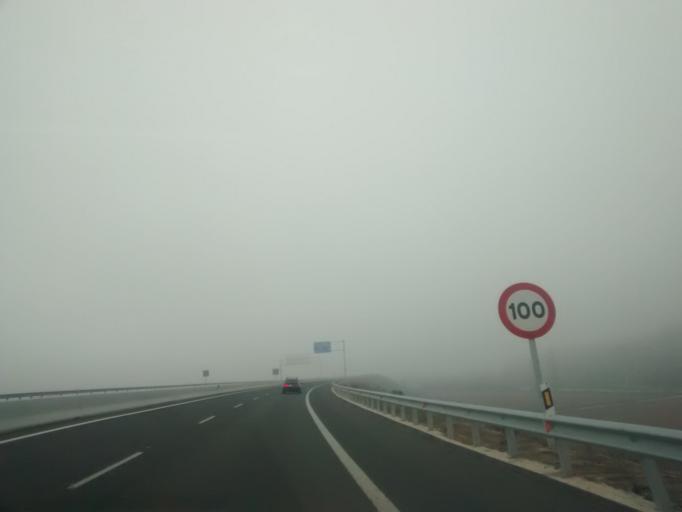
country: ES
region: La Rioja
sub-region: Provincia de La Rioja
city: Murillo de Rio Leza
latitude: 42.4524
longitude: -2.3576
